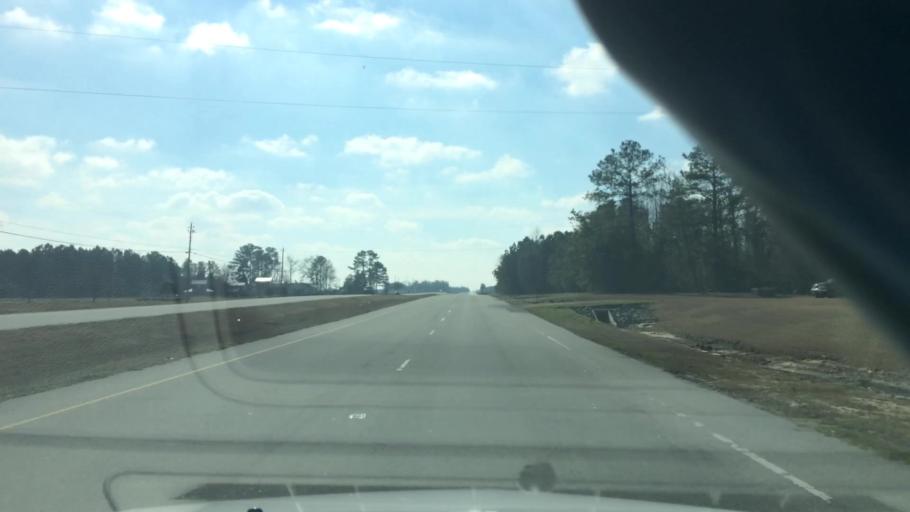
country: US
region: North Carolina
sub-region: Duplin County
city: Beulaville
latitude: 35.1060
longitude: -77.7211
